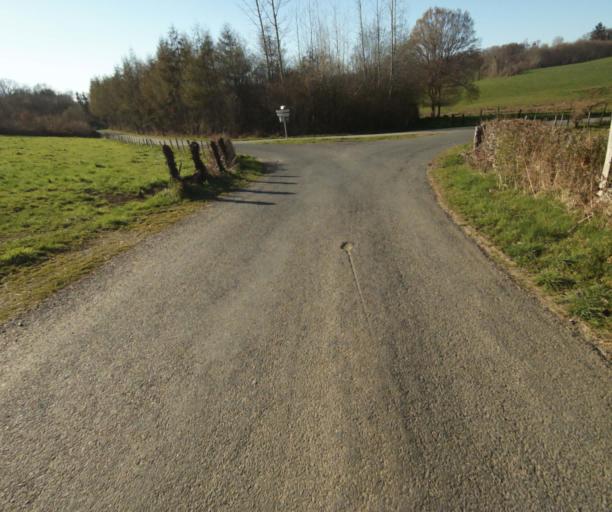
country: FR
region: Limousin
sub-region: Departement de la Correze
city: Seilhac
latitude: 45.3810
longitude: 1.7101
